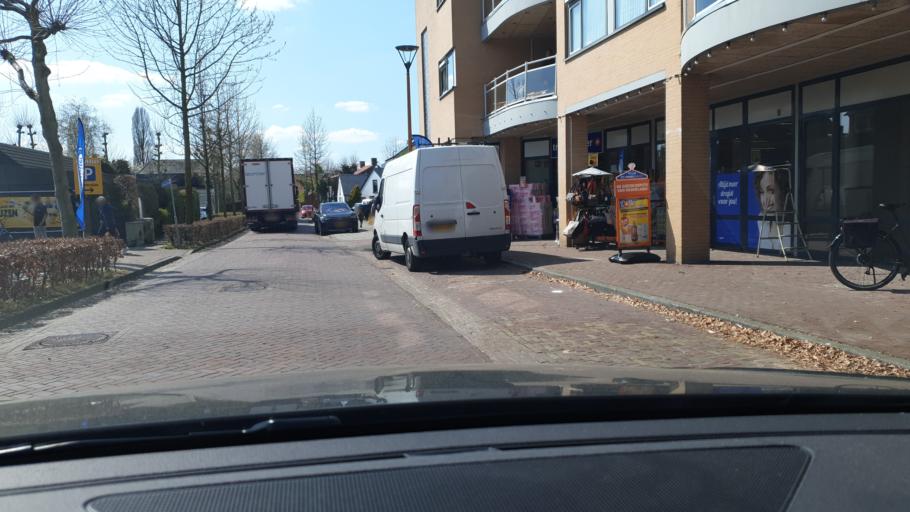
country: NL
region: North Brabant
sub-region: Gemeente Bladel en Netersel
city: Bladel
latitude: 51.3697
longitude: 5.2520
